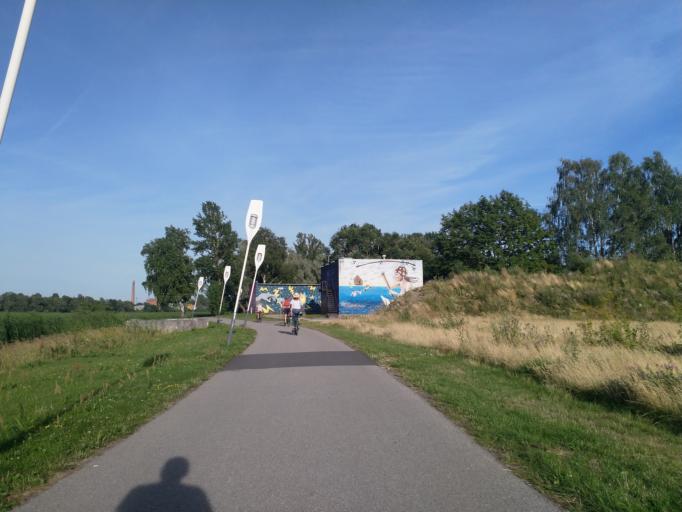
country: EE
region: Paernumaa
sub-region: Paernu linn
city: Parnu
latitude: 58.3888
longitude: 24.5104
